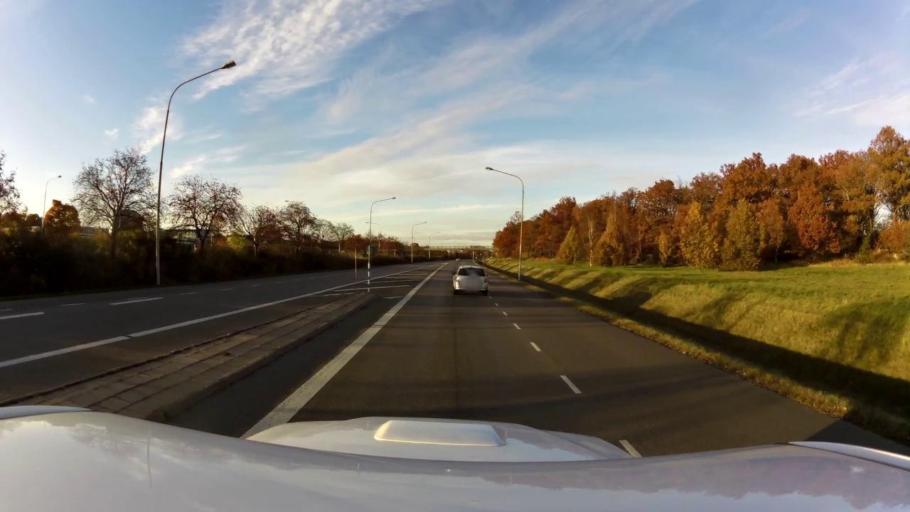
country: SE
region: OEstergoetland
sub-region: Linkopings Kommun
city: Sturefors
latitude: 58.3803
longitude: 15.6840
